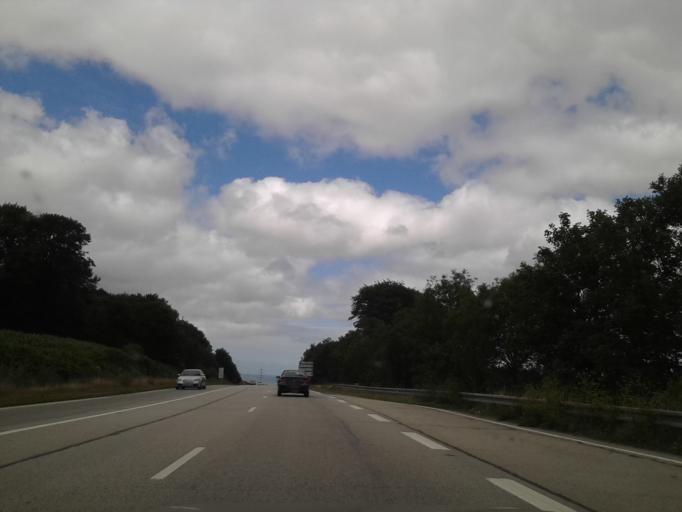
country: FR
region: Lower Normandy
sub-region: Departement de la Manche
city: La Glacerie
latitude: 49.6142
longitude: -1.5830
